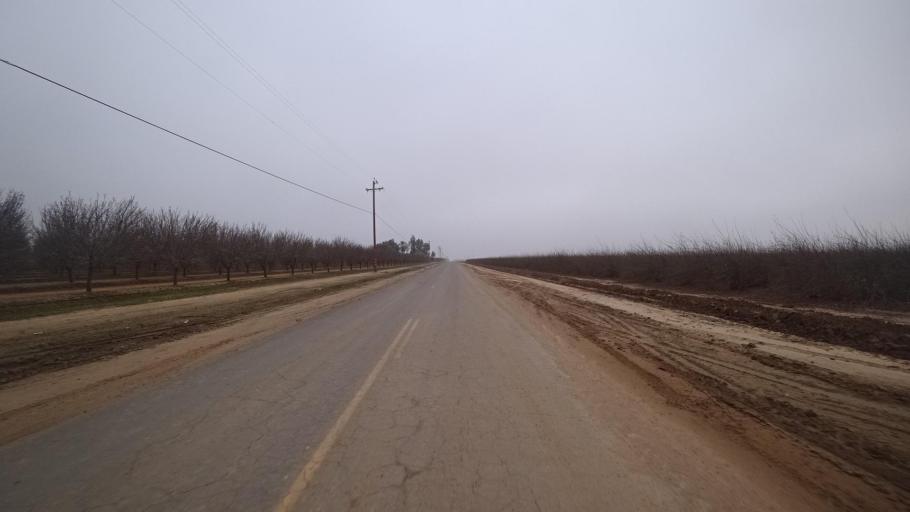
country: US
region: California
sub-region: Kern County
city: Lost Hills
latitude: 35.6004
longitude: -119.5268
